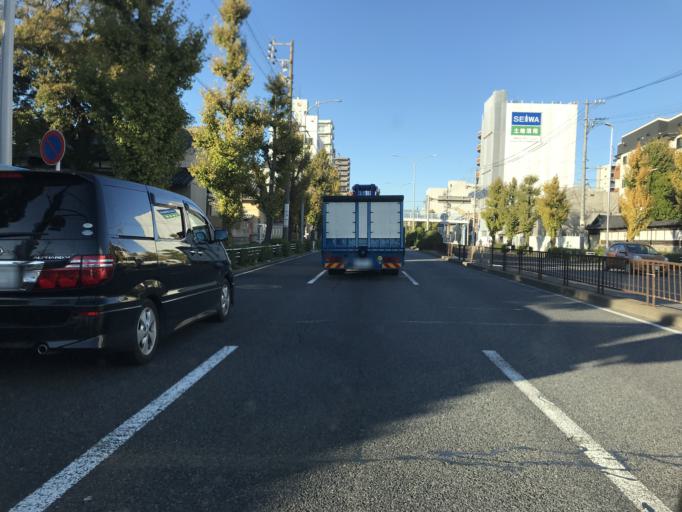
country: JP
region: Aichi
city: Nagoya-shi
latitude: 35.1725
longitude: 136.8728
